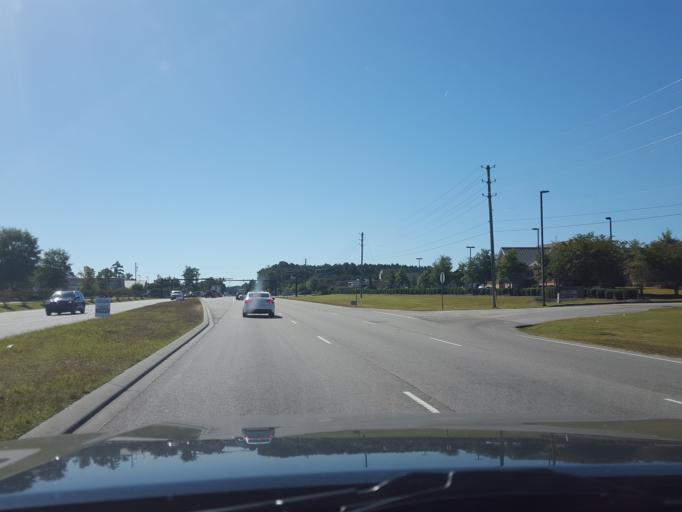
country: US
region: North Carolina
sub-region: New Hanover County
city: Seagate
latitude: 34.2373
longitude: -77.8285
